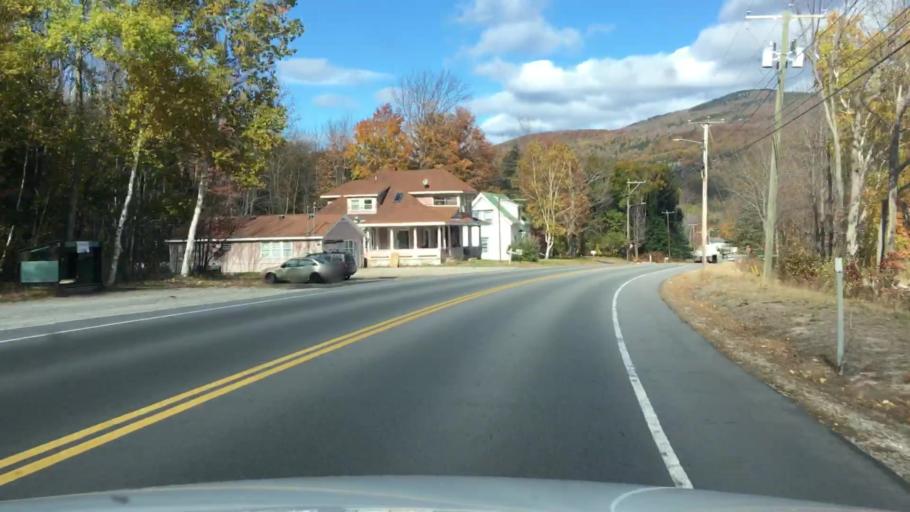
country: US
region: New Hampshire
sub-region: Coos County
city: Gorham
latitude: 44.3807
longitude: -71.1736
